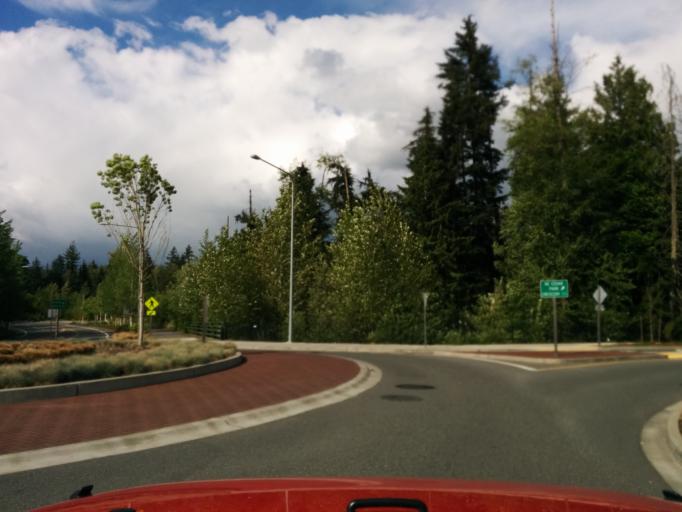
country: US
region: Washington
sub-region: King County
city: Union Hill-Novelty Hill
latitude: 47.6855
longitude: -122.0327
